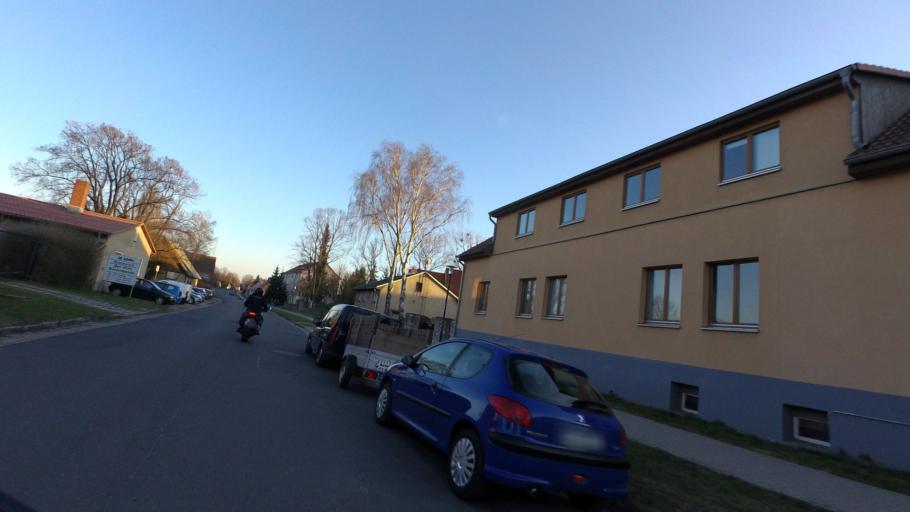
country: DE
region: Berlin
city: Hellersdorf
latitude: 52.5476
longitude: 13.6368
